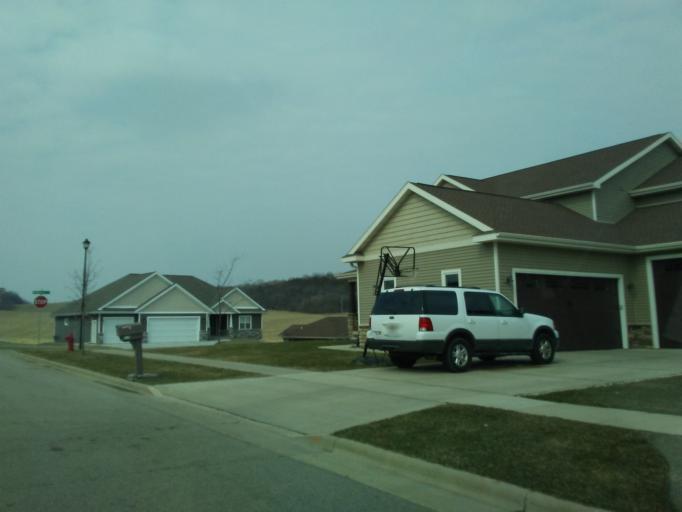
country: US
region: Wisconsin
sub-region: Columbia County
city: Lodi
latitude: 43.3090
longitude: -89.5510
